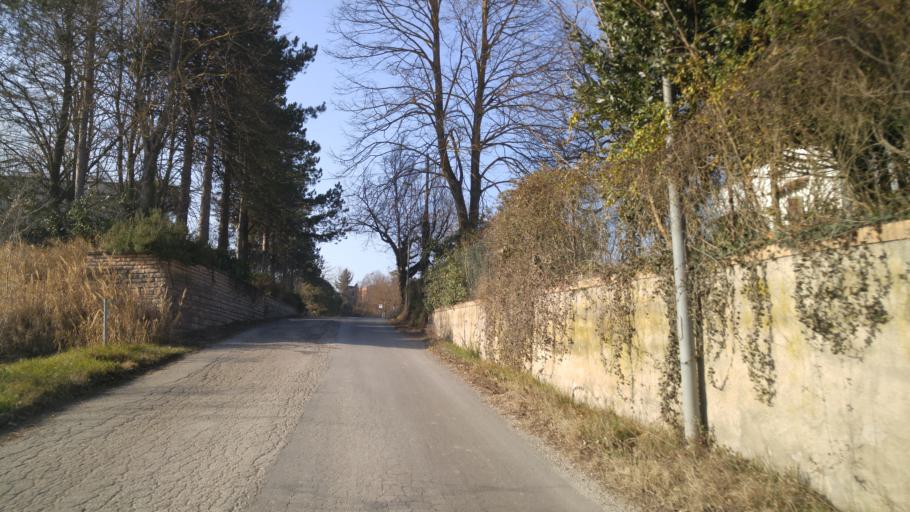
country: IT
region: The Marches
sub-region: Provincia di Pesaro e Urbino
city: Fenile
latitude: 43.8286
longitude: 12.9175
